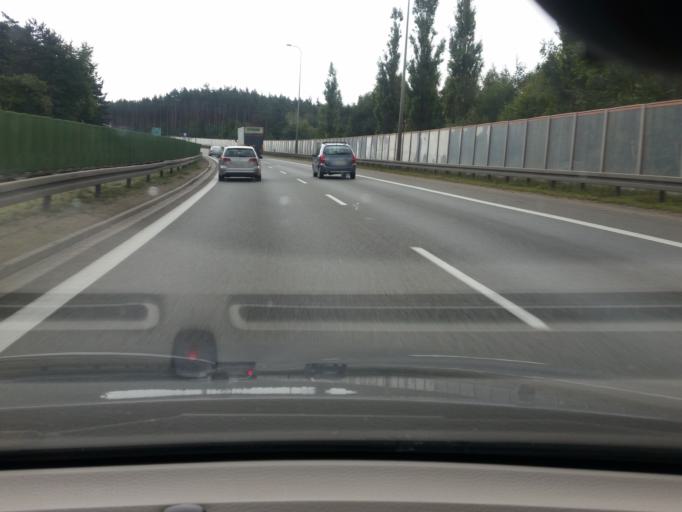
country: PL
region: Pomeranian Voivodeship
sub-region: Powiat gdanski
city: Rotmanka
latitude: 54.2713
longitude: 18.5954
